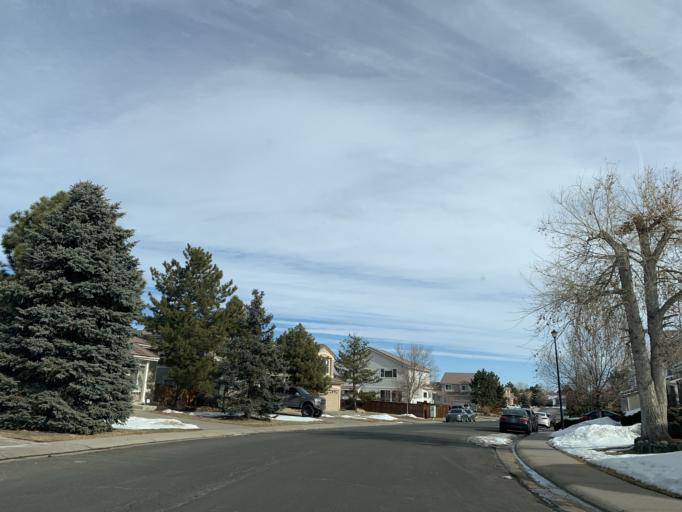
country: US
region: Colorado
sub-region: Douglas County
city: Carriage Club
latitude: 39.5362
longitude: -104.9364
